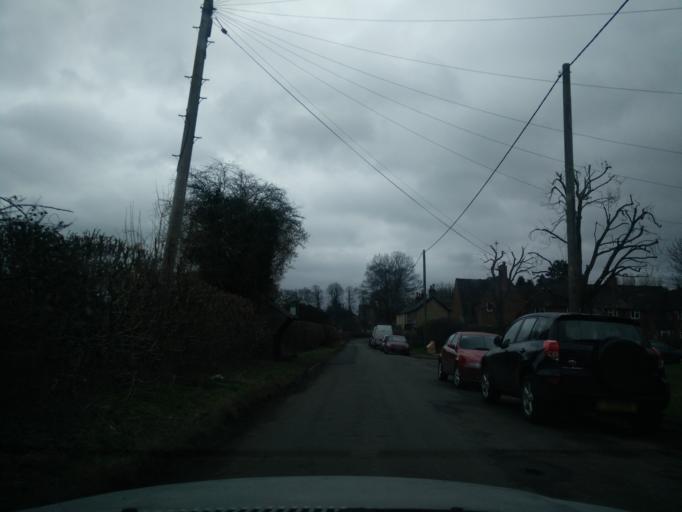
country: GB
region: England
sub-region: Buckinghamshire
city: Great Missenden
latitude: 51.6827
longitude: -0.6730
